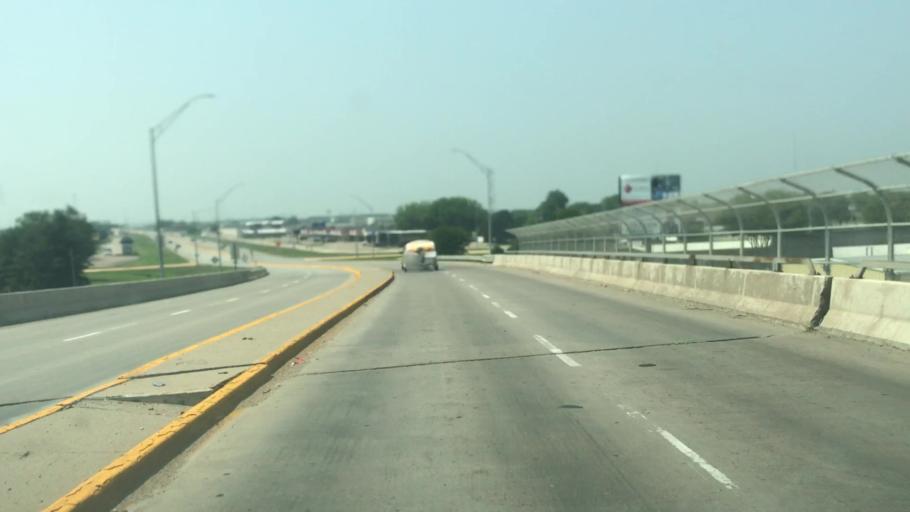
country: US
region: Nebraska
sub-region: Hall County
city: Grand Island
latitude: 40.9155
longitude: -98.3673
